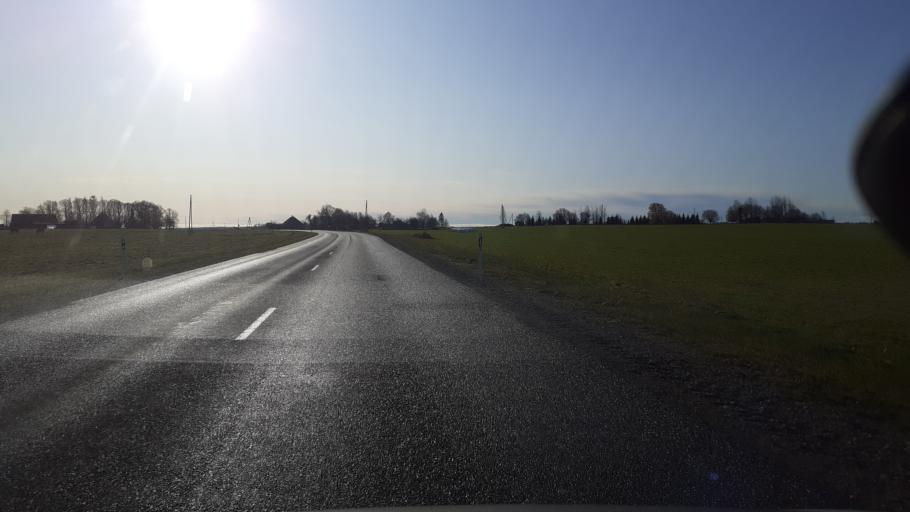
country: LV
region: Kuldigas Rajons
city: Kuldiga
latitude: 57.0149
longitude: 21.8768
